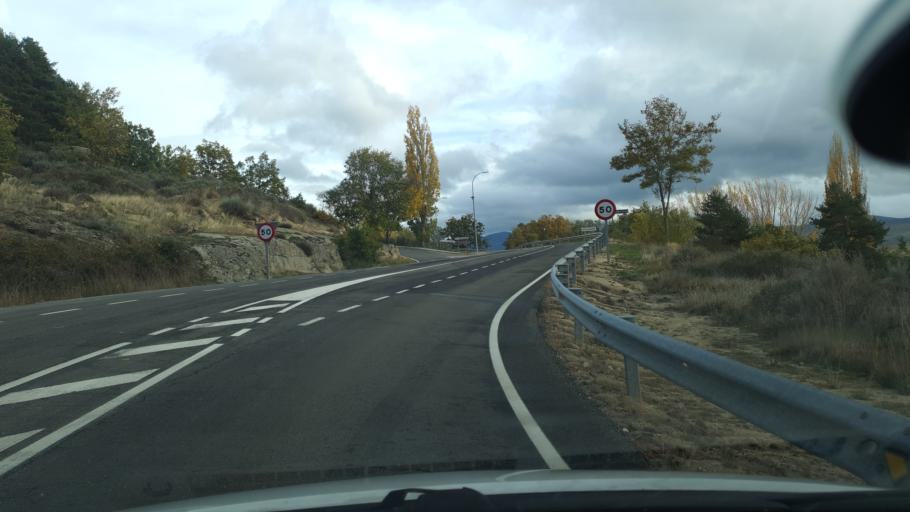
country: ES
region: Castille and Leon
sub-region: Provincia de Avila
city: Hoyocasero
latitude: 40.4004
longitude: -4.9842
